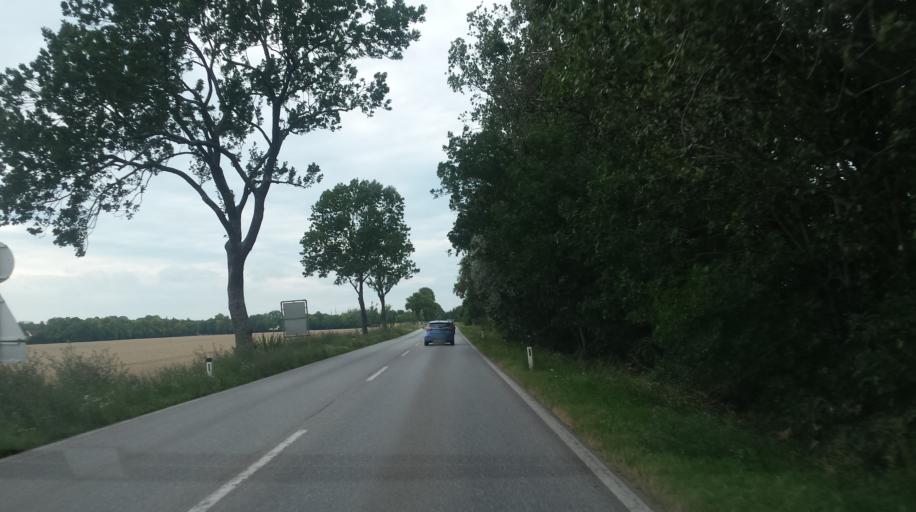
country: AT
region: Lower Austria
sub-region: Politischer Bezirk Wien-Umgebung
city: Moosbrunn
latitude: 48.0539
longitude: 16.4604
